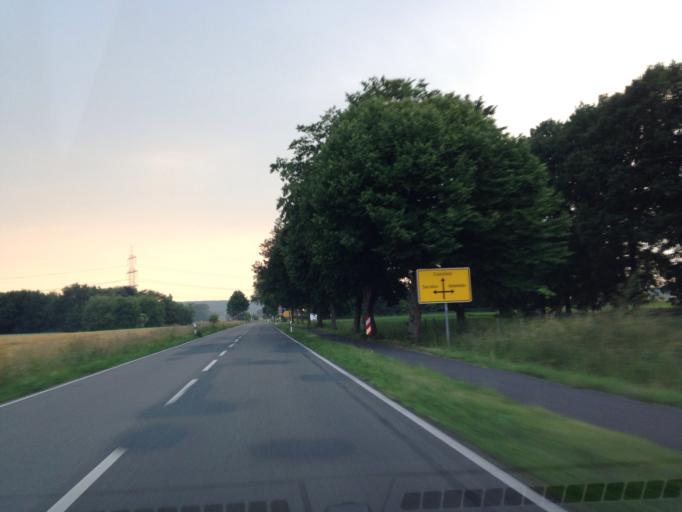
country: DE
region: North Rhine-Westphalia
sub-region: Regierungsbezirk Munster
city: Havixbeck
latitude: 51.9690
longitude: 7.4712
